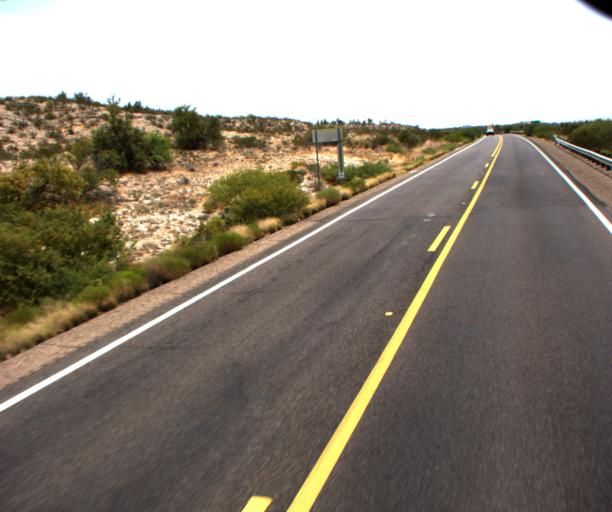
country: US
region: Arizona
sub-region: Gila County
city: Peridot
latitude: 33.2757
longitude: -110.3285
